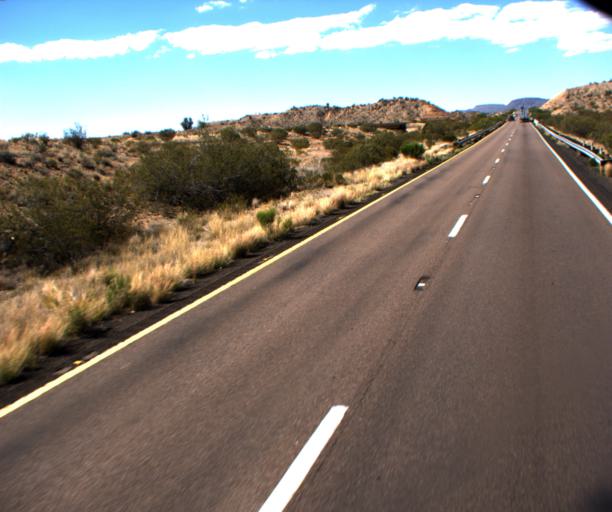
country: US
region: Arizona
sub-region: Mohave County
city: Kingman
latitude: 35.0757
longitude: -113.6652
